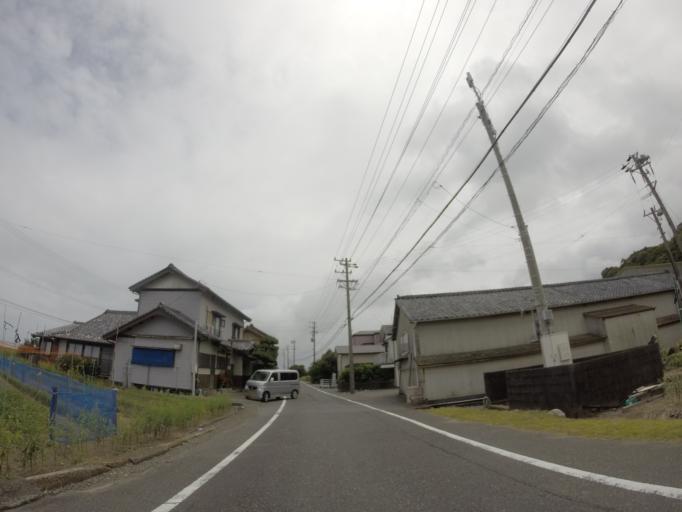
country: JP
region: Shizuoka
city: Sagara
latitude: 34.7110
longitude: 138.2132
